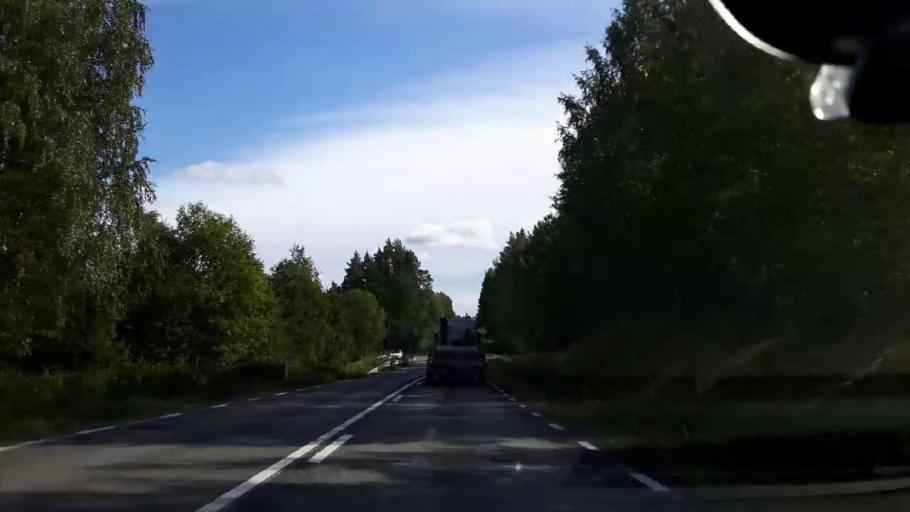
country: SE
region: Jaemtland
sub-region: Braecke Kommun
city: Braecke
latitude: 63.1942
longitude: 15.4179
